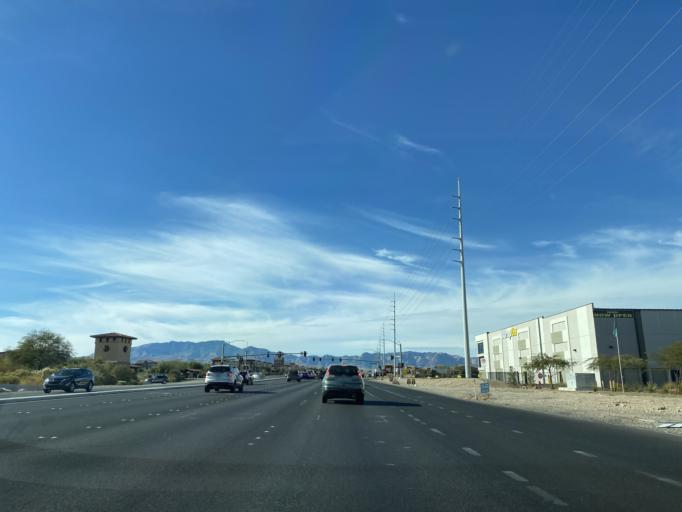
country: US
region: Nevada
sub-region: Clark County
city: Enterprise
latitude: 36.0203
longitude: -115.2592
